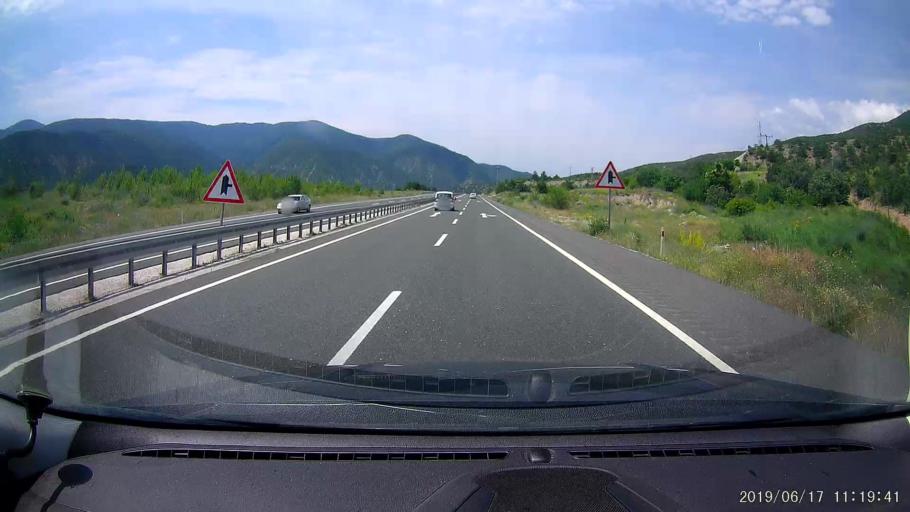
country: TR
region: Cankiri
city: Yaprakli
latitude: 40.9237
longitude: 33.8224
